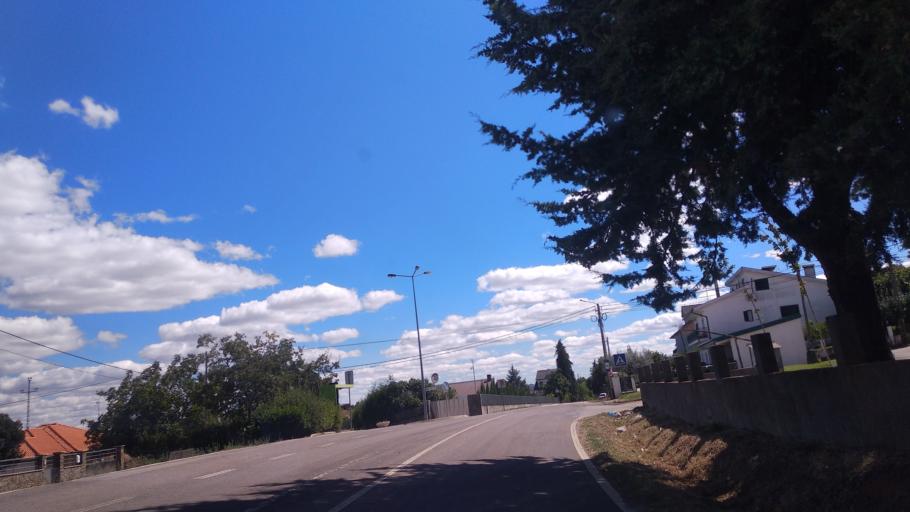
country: PT
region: Braganca
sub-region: Braganca Municipality
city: Braganca
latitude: 41.7792
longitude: -6.7630
